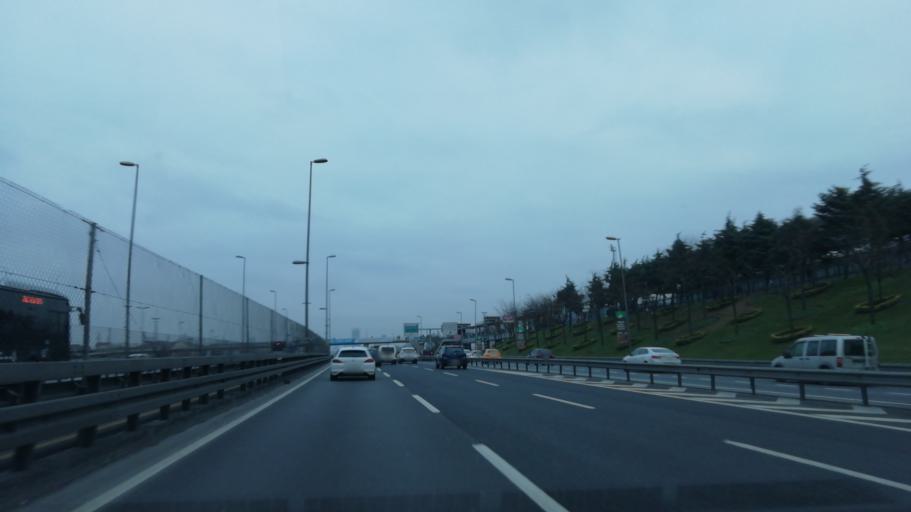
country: TR
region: Istanbul
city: Sisli
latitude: 41.0543
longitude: 28.9572
